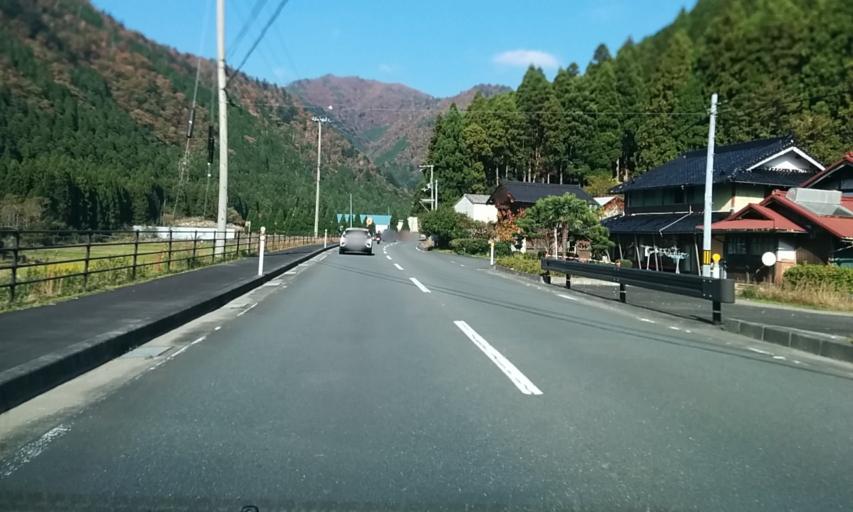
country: JP
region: Fukui
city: Obama
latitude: 35.2916
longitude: 135.6008
